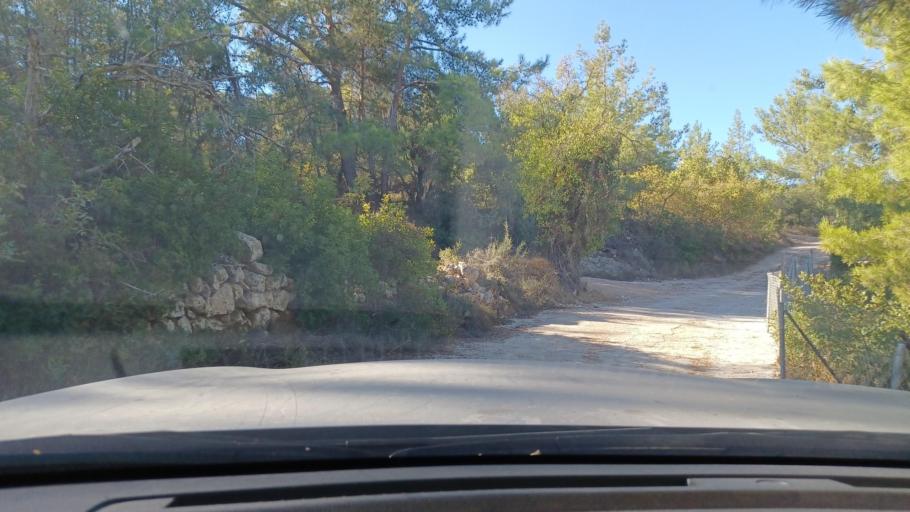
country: CY
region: Pafos
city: Polis
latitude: 34.9981
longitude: 32.5201
